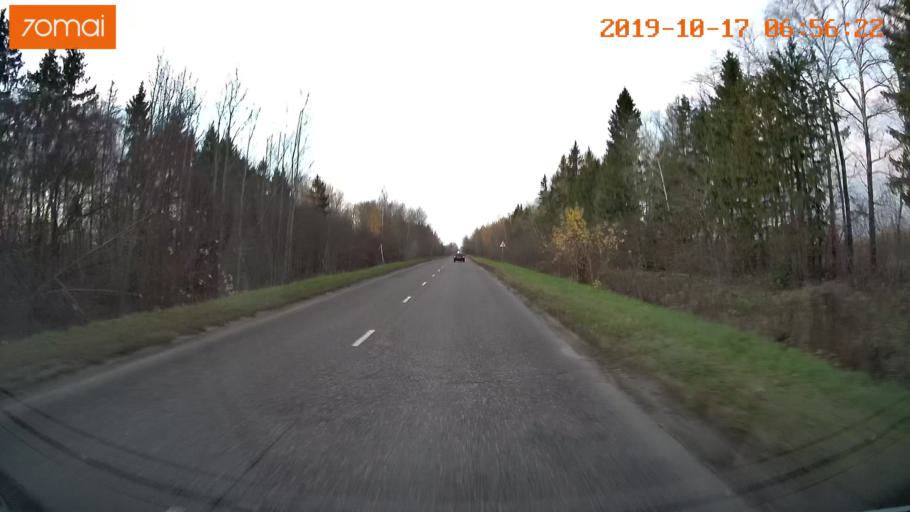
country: RU
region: Vladimir
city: Suzdal'
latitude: 56.4474
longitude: 40.4485
